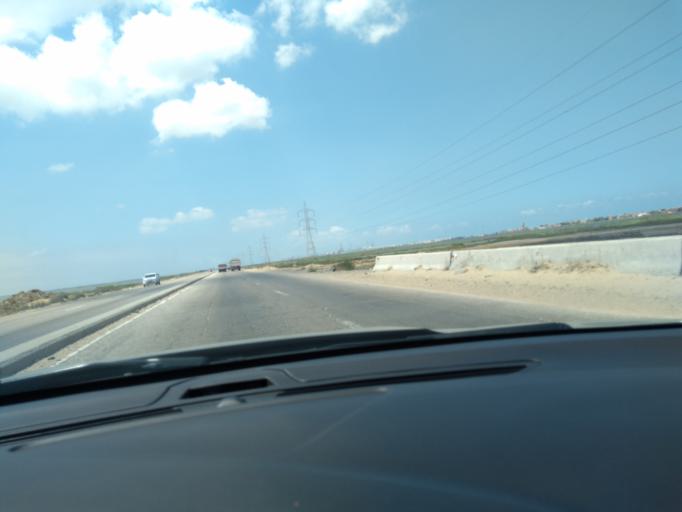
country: EG
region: Muhafazat Bur Sa`id
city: Port Said
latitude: 31.2743
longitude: 32.2033
